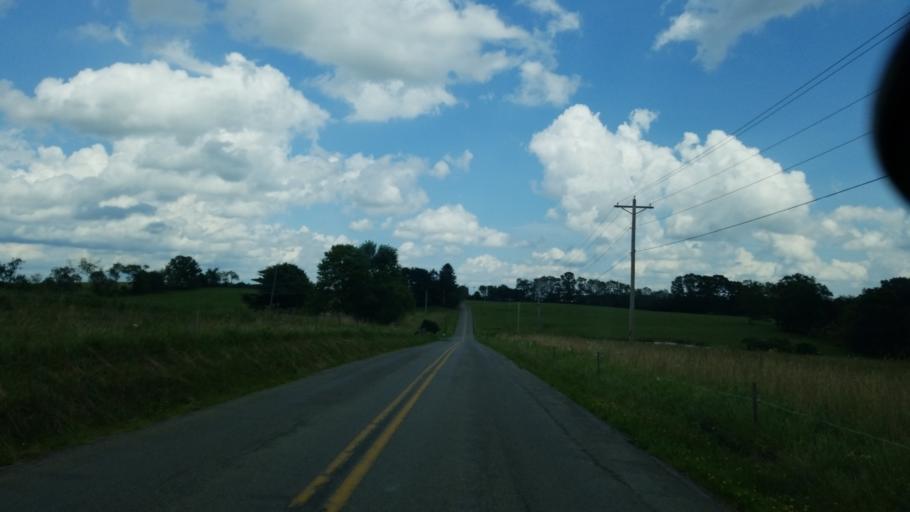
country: US
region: Pennsylvania
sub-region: Jefferson County
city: Brookville
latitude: 41.2390
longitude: -79.0343
